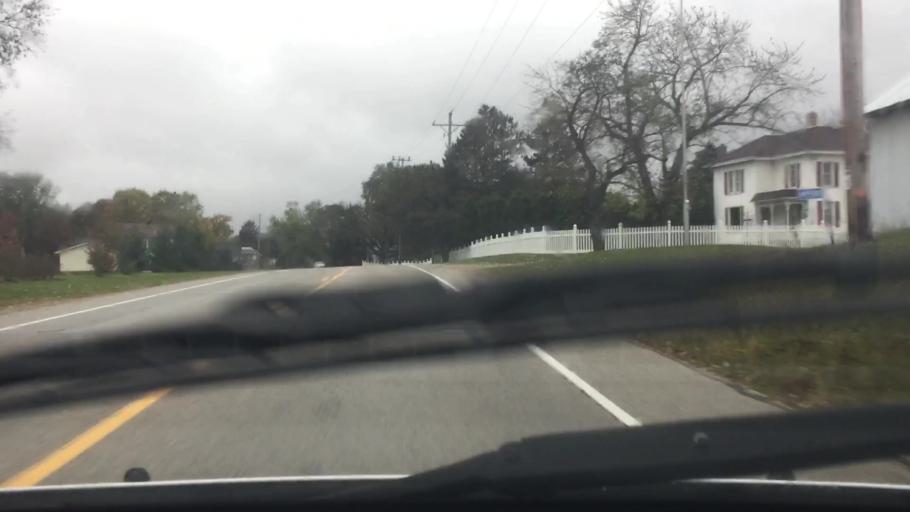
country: US
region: Wisconsin
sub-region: Jefferson County
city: Palmyra
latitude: 42.8399
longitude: -88.5377
